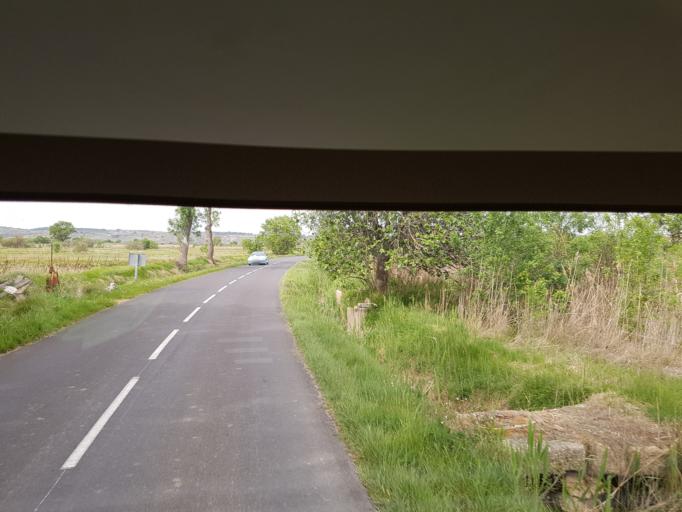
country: FR
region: Languedoc-Roussillon
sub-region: Departement de l'Aude
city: Fleury
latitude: 43.2508
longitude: 3.1547
